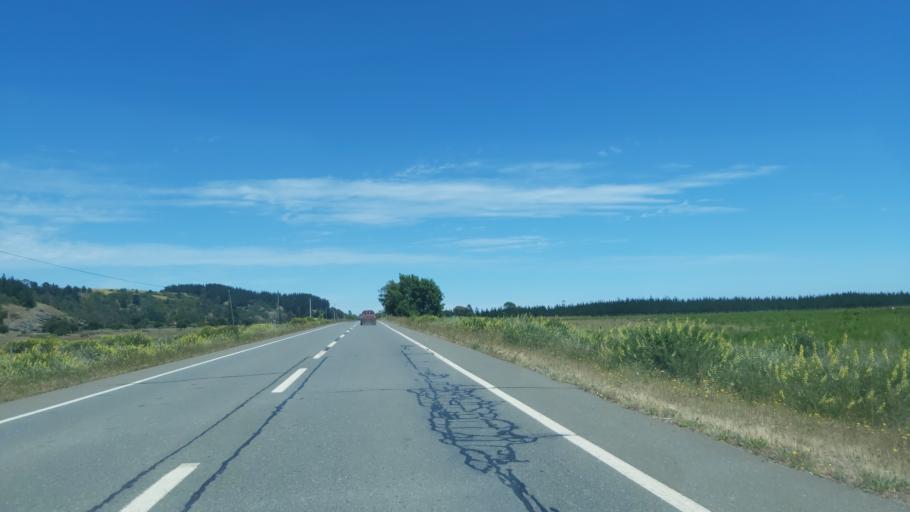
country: CL
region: Maule
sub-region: Provincia de Talca
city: Constitucion
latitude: -35.1627
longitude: -72.2574
